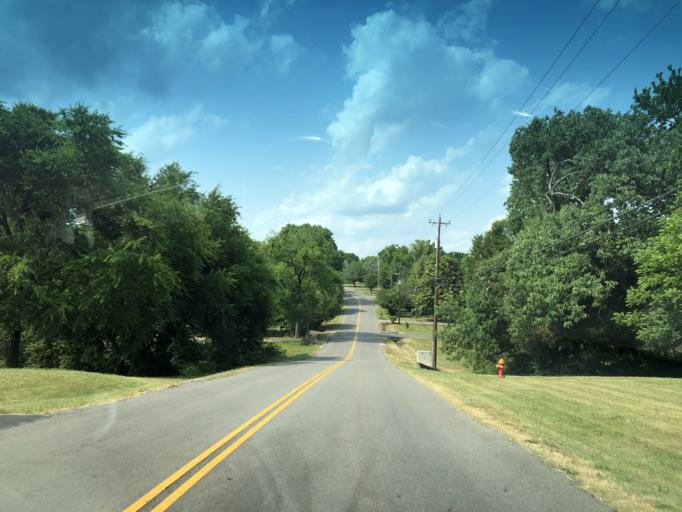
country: US
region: Tennessee
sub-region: Davidson County
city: Goodlettsville
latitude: 36.2496
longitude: -86.7285
